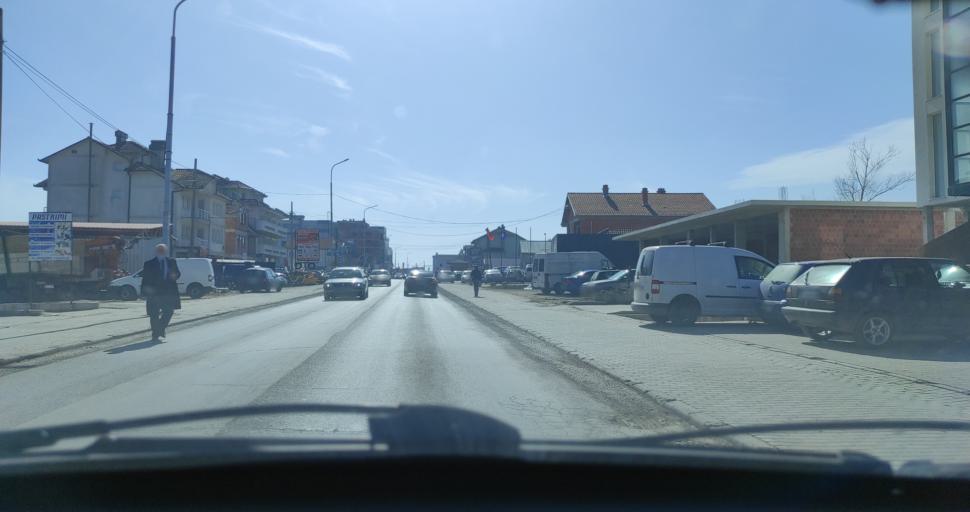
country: XK
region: Gjakova
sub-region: Komuna e Decanit
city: Decan
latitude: 42.5470
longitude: 20.2904
